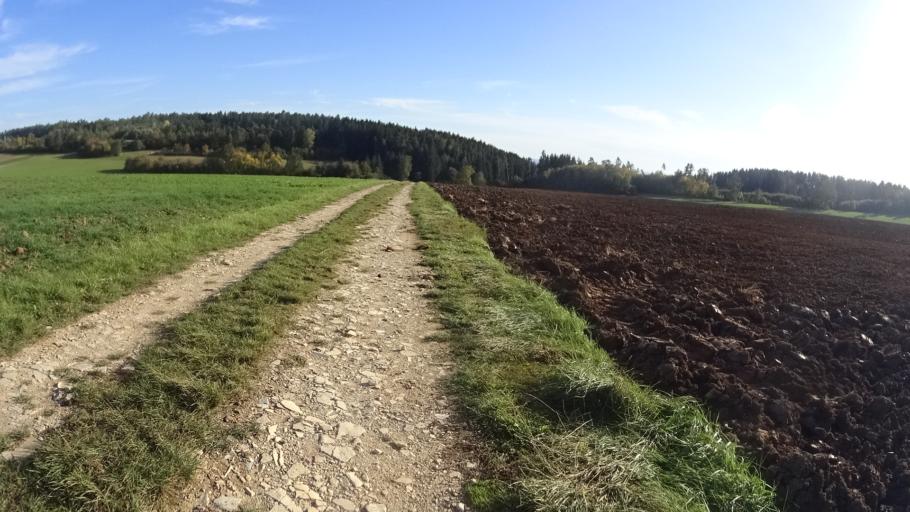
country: DE
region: Bavaria
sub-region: Upper Bavaria
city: Bohmfeld
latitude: 48.8533
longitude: 11.3621
